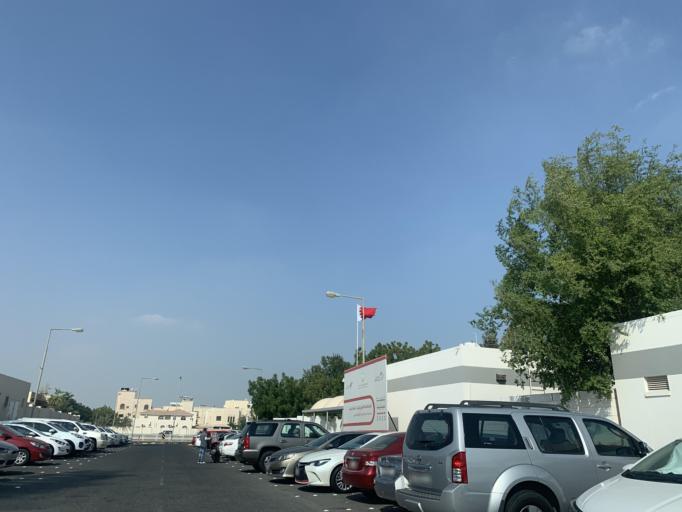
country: BH
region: Central Governorate
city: Madinat Hamad
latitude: 26.1328
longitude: 50.4956
